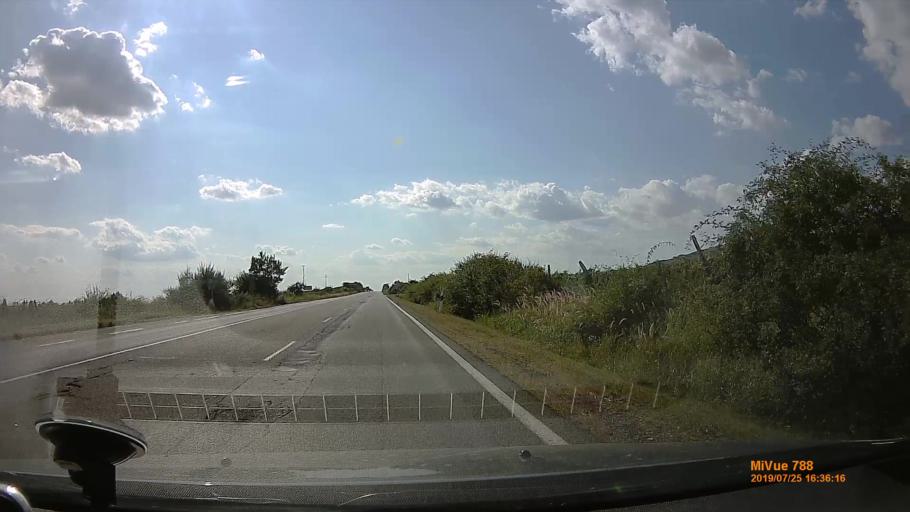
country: HU
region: Heves
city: Abasar
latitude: 47.7688
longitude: 19.9855
